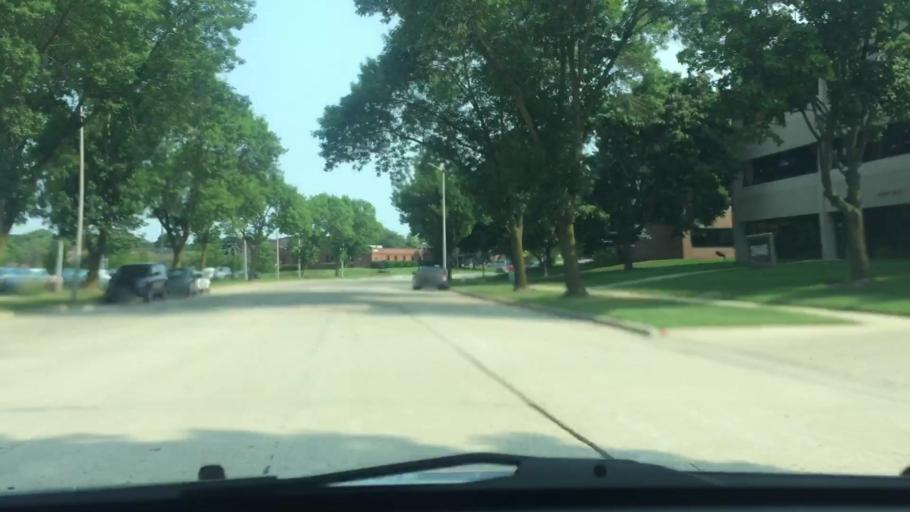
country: US
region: Wisconsin
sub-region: Milwaukee County
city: West Allis
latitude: 42.9992
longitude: -88.0419
